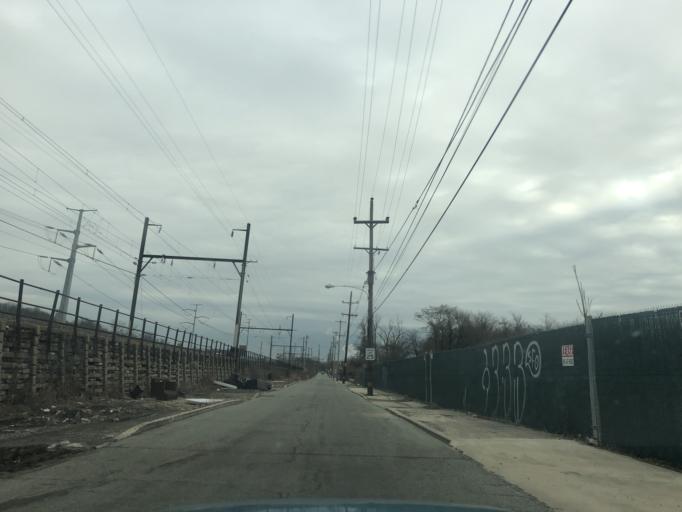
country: US
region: Pennsylvania
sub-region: Montgomery County
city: Bridgeport
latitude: 40.1109
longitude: -75.3395
